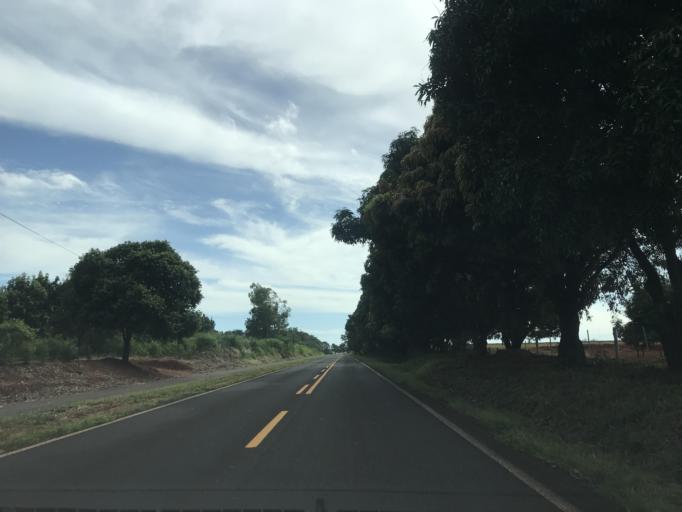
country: BR
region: Parana
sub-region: Terra Rica
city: Terra Rica
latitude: -22.7558
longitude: -52.6292
